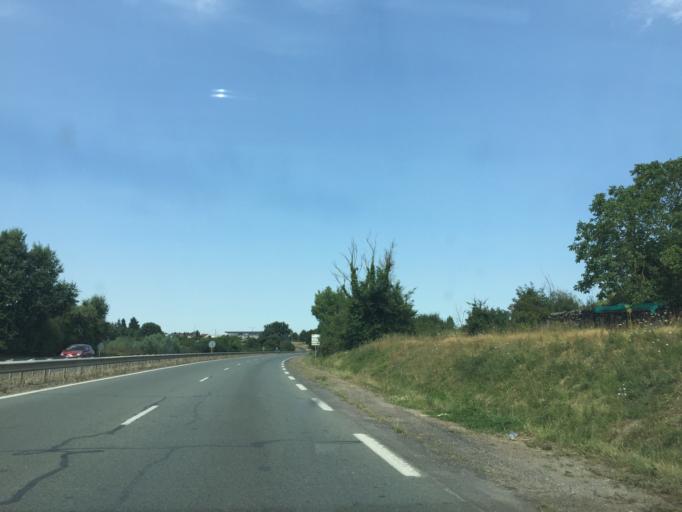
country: FR
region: Poitou-Charentes
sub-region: Departement de la Vienne
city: Biard
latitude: 46.5584
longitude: 0.3031
